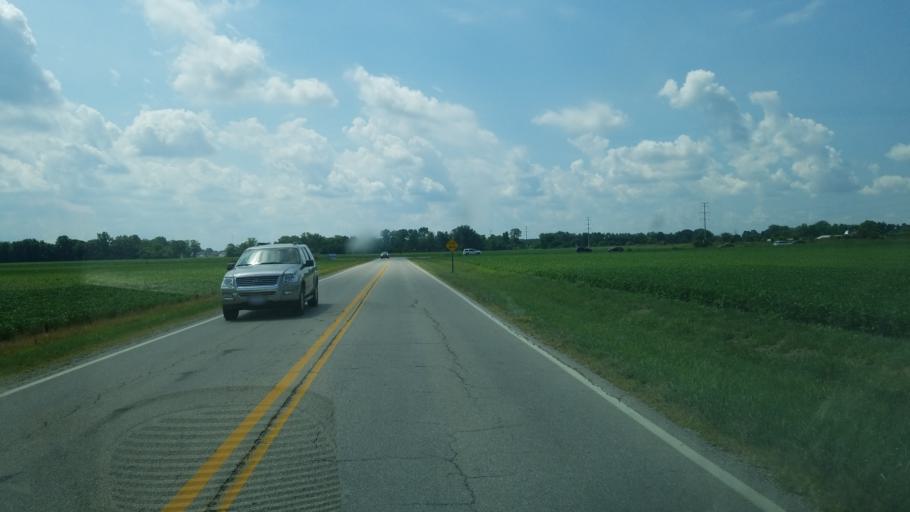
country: US
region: Ohio
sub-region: Delaware County
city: Lewis Center
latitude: 40.2147
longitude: -83.0077
